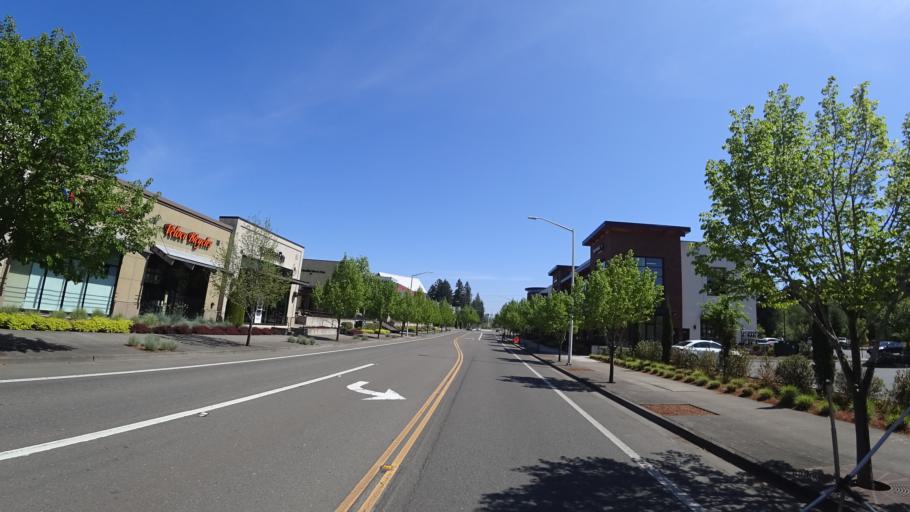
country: US
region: Oregon
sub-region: Washington County
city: King City
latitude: 45.4296
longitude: -122.8298
